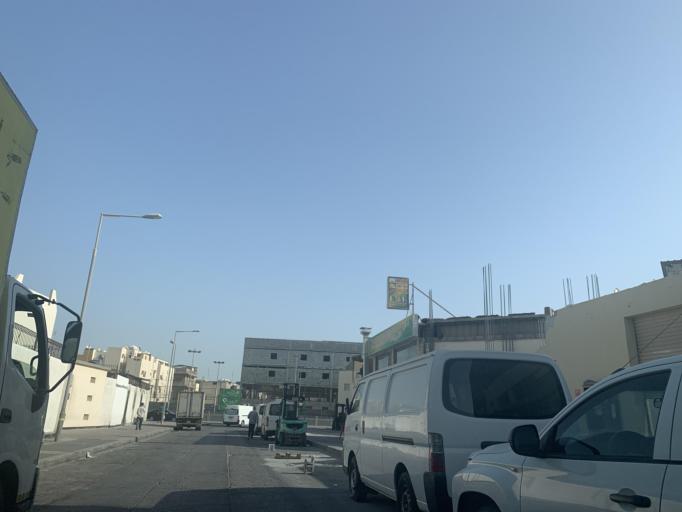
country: BH
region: Manama
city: Manama
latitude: 26.2295
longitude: 50.5669
